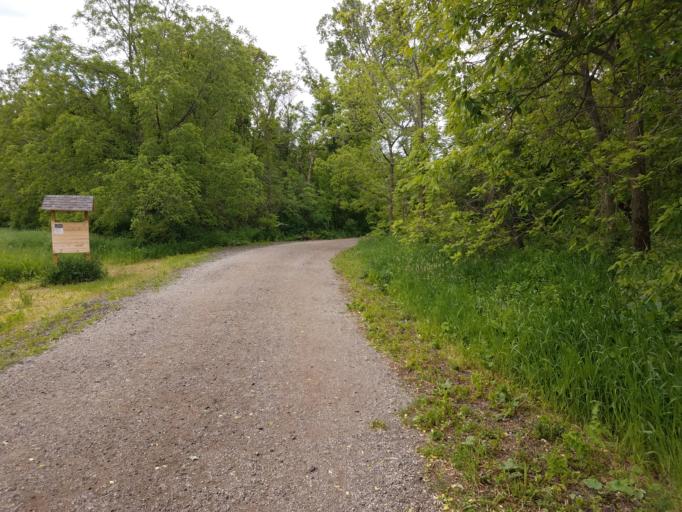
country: US
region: Minnesota
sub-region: Olmsted County
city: Rochester
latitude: 43.9554
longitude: -92.4380
